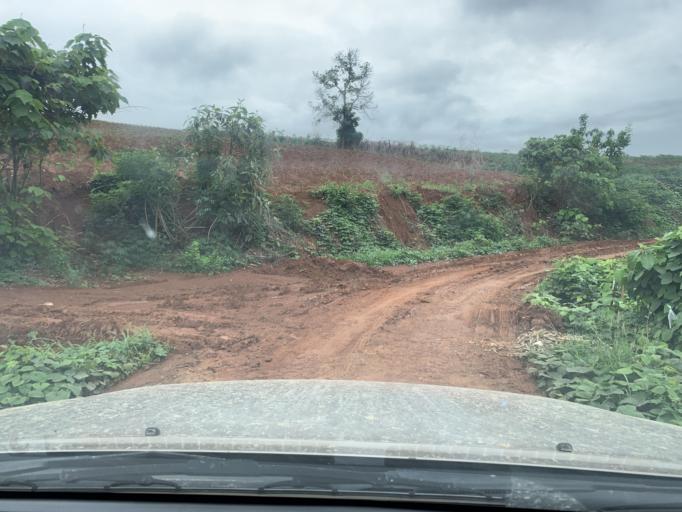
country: TH
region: Nan
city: Mae Charim
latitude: 18.4073
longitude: 101.4417
